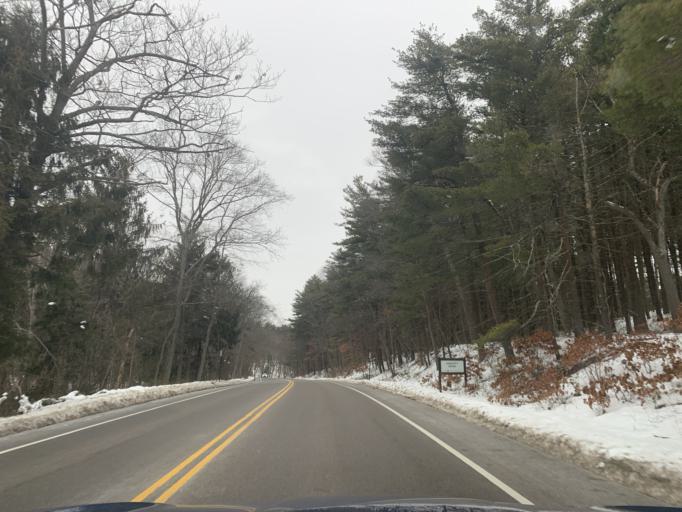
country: US
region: Massachusetts
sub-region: Norfolk County
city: Milton
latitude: 42.2162
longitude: -71.0919
